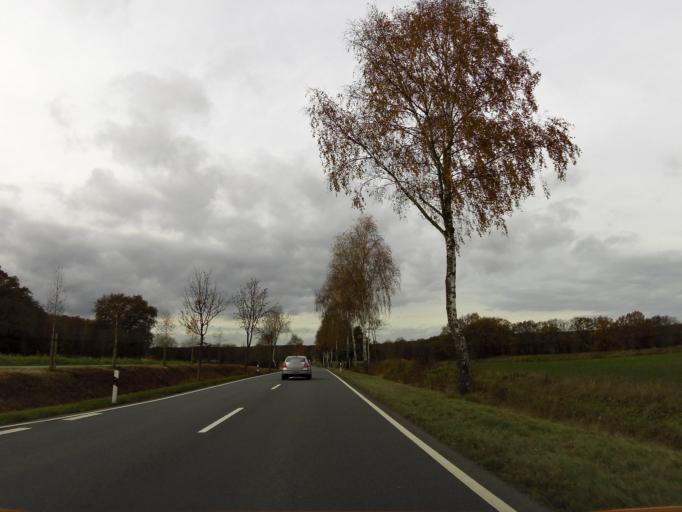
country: DE
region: Lower Saxony
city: Bergen an der Dumme
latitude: 52.8970
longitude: 10.9381
